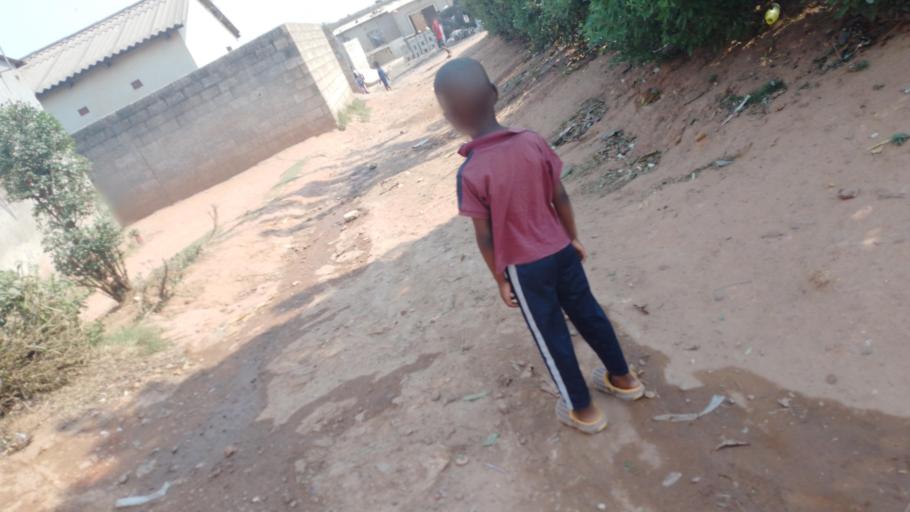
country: ZM
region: Lusaka
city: Lusaka
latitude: -15.3997
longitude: 28.3670
